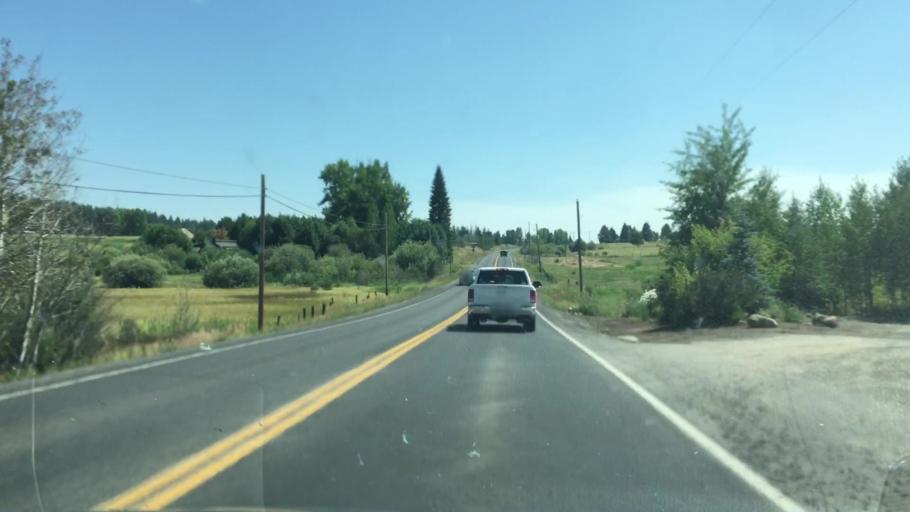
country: US
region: Idaho
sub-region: Valley County
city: McCall
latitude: 44.8899
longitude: -116.0931
